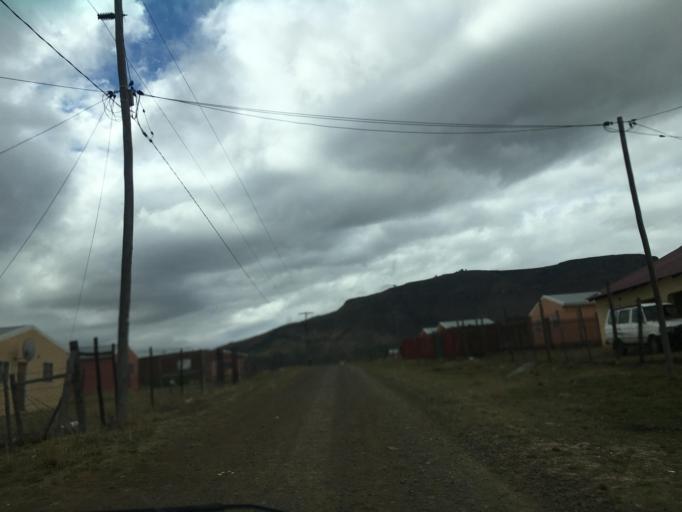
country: ZA
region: Eastern Cape
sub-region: Chris Hani District Municipality
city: Cala
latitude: -31.5412
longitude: 27.6982
